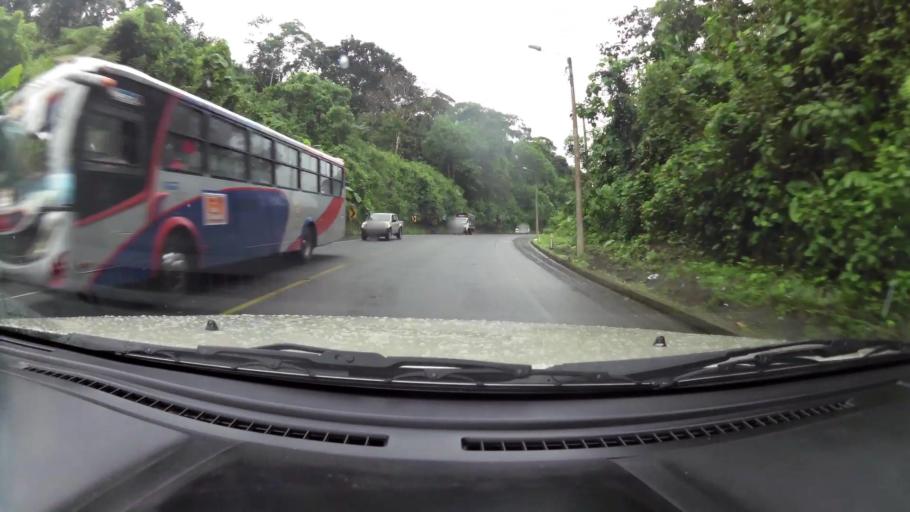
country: EC
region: Santo Domingo de los Tsachilas
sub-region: Canton Santo Domingo de los Colorados
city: Santo Domingo de los Colorados
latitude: -0.2491
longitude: -79.1410
